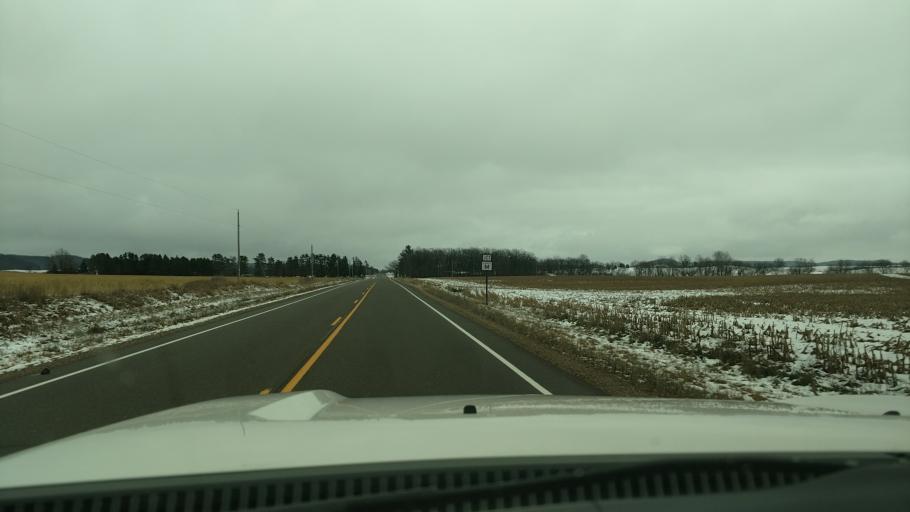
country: US
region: Wisconsin
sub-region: Dunn County
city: Colfax
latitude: 45.1427
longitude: -91.7017
